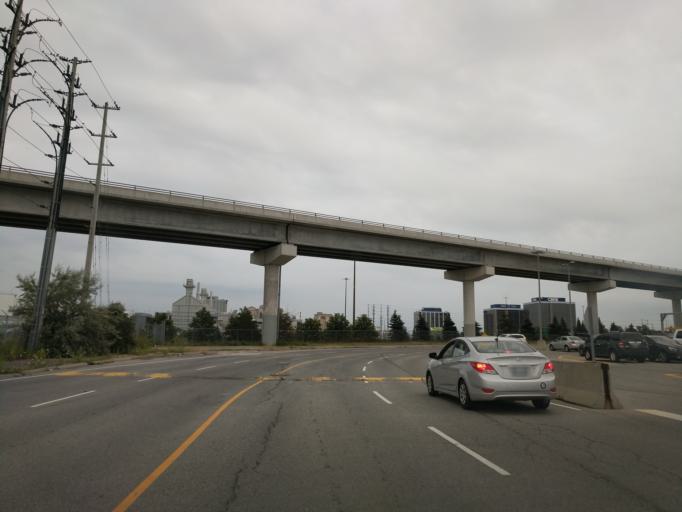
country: CA
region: Ontario
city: Etobicoke
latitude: 43.6929
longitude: -79.6133
